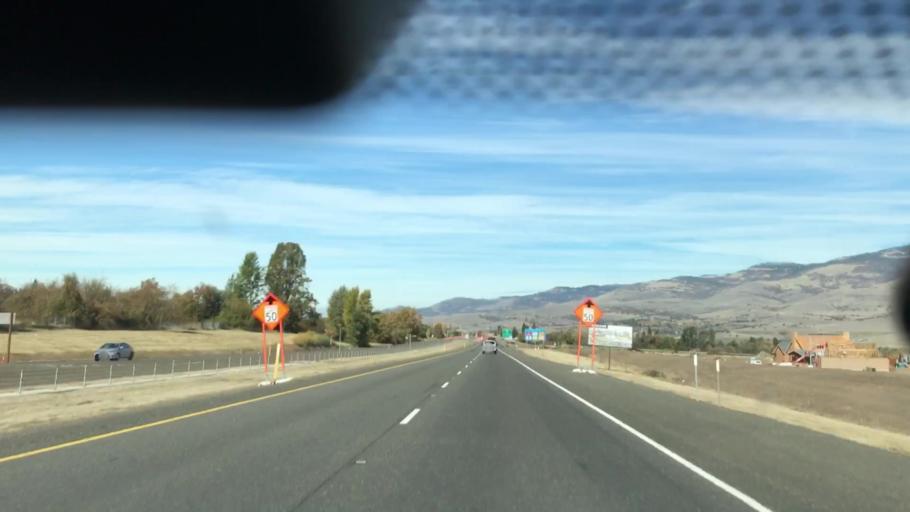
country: US
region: Oregon
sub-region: Jackson County
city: Ashland
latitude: 42.1650
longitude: -122.6523
